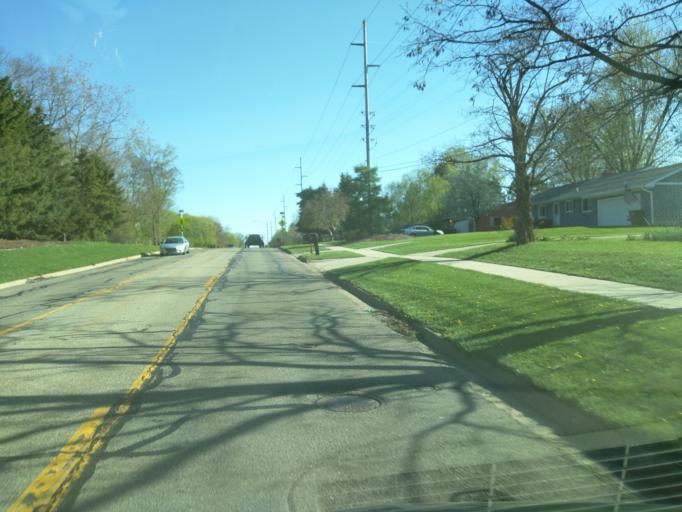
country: US
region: Michigan
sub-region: Eaton County
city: Waverly
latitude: 42.7492
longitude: -84.6423
